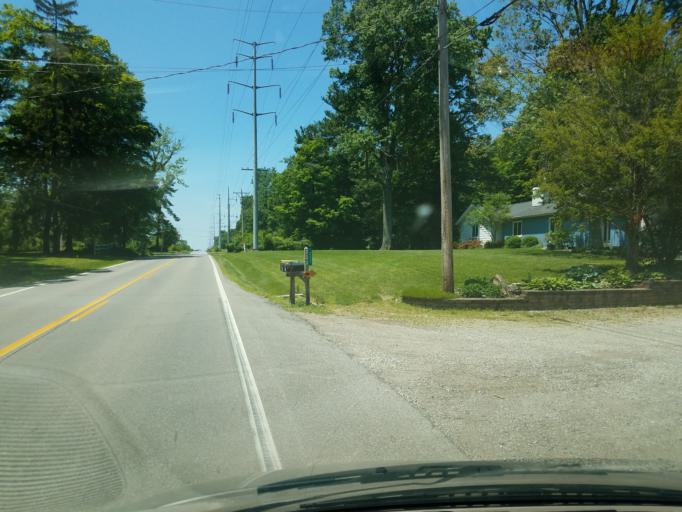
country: US
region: Ohio
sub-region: Delaware County
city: Lewis Center
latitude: 40.2140
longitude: -83.0369
